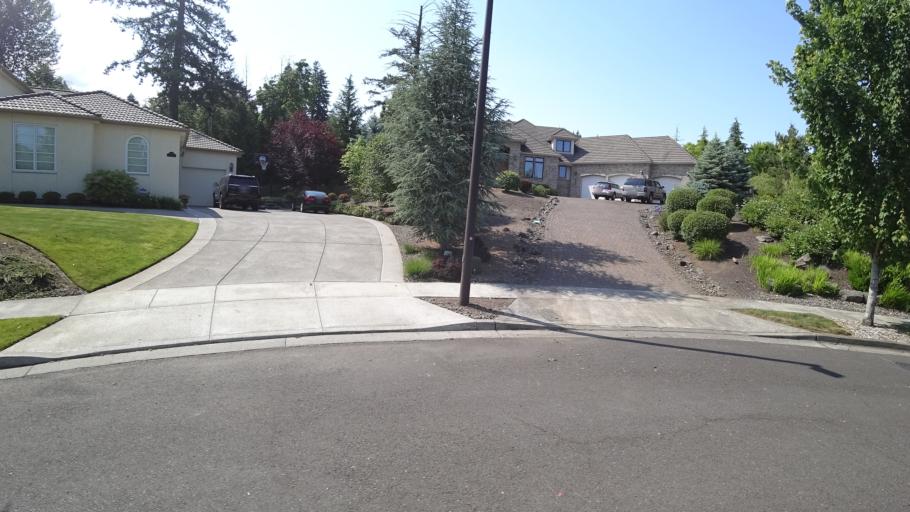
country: US
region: Oregon
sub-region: Clackamas County
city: Happy Valley
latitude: 45.4464
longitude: -122.5350
